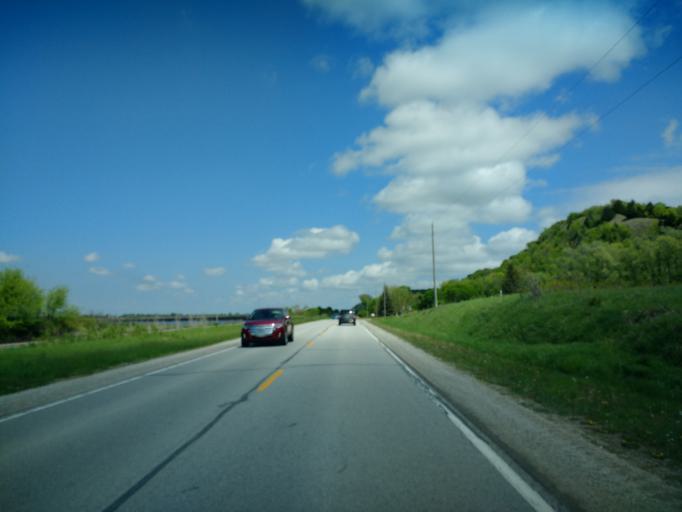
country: US
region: Iowa
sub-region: Harrison County
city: Missouri Valley
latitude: 41.4544
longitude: -95.8742
